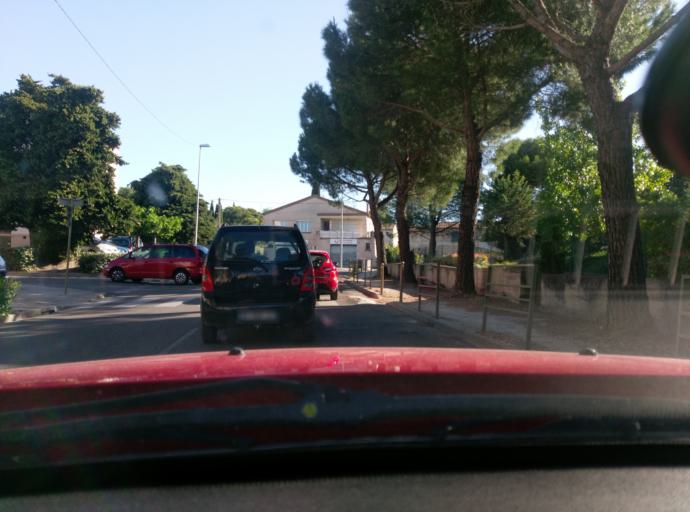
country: FR
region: Languedoc-Roussillon
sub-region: Departement du Gard
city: Uzes
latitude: 44.0139
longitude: 4.4146
